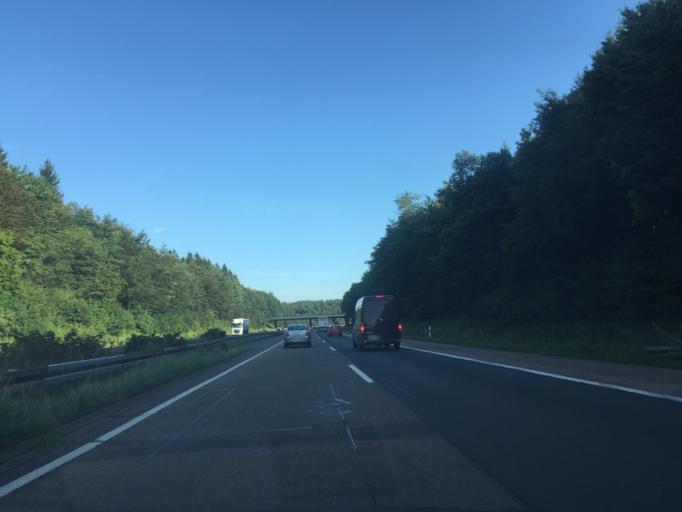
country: DE
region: North Rhine-Westphalia
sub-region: Regierungsbezirk Arnsberg
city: Luedenscheid
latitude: 51.1672
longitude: 7.6565
